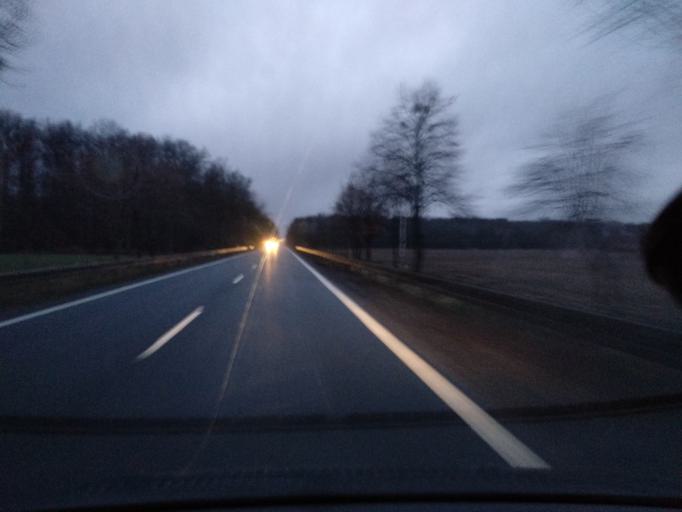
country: PL
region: Lower Silesian Voivodeship
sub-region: Powiat sredzki
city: Ciechow
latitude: 51.1746
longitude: 16.5372
